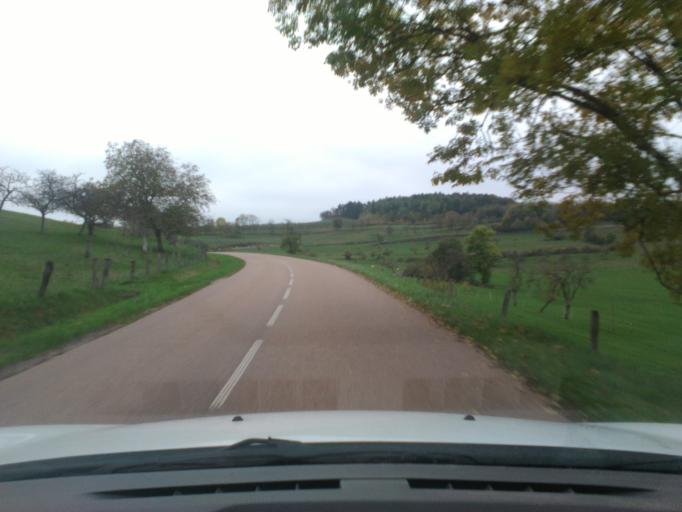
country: FR
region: Lorraine
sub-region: Departement des Vosges
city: Vincey
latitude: 48.3003
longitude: 6.2666
